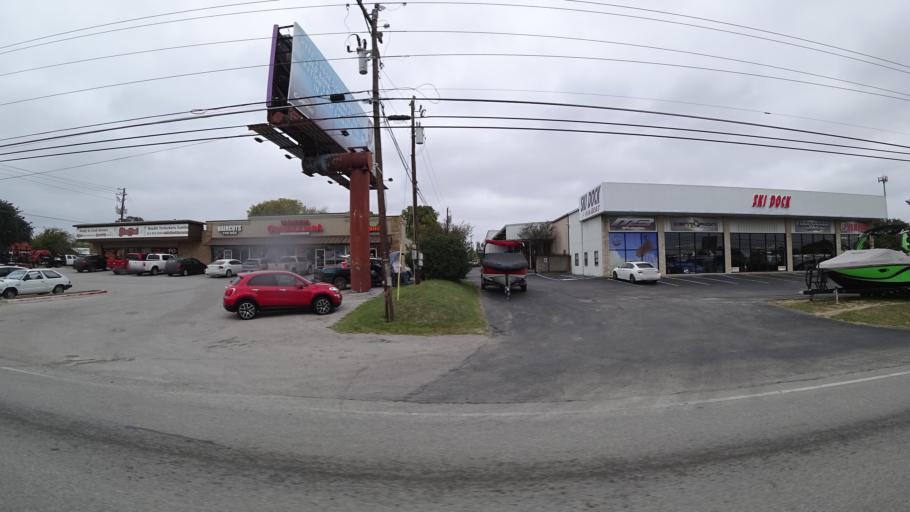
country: US
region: Texas
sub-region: Williamson County
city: Anderson Mill
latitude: 30.4624
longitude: -97.8153
